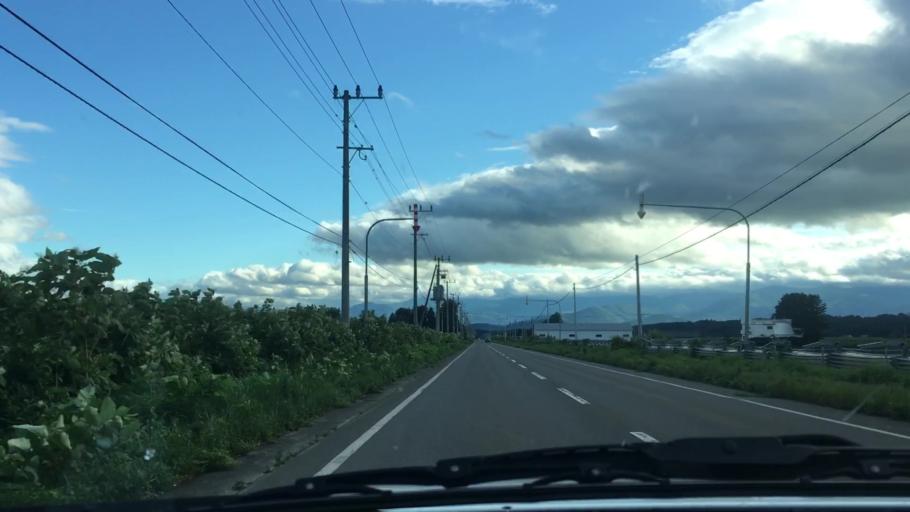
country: JP
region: Hokkaido
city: Otofuke
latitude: 43.1560
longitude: 142.9023
